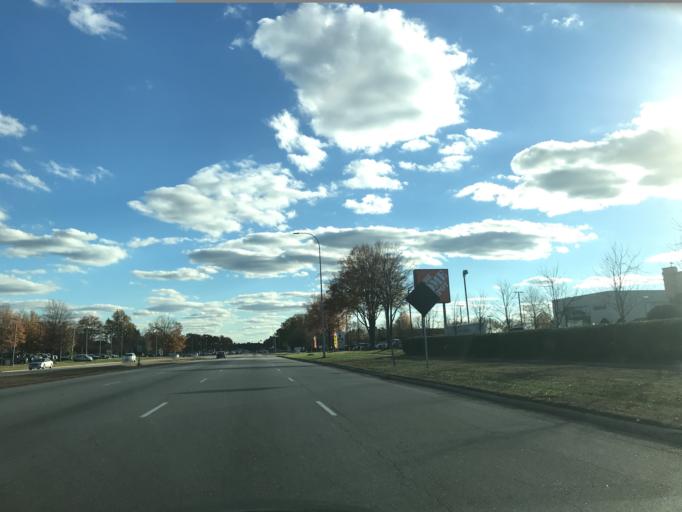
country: US
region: North Carolina
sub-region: Wake County
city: Raleigh
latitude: 35.8530
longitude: -78.5810
